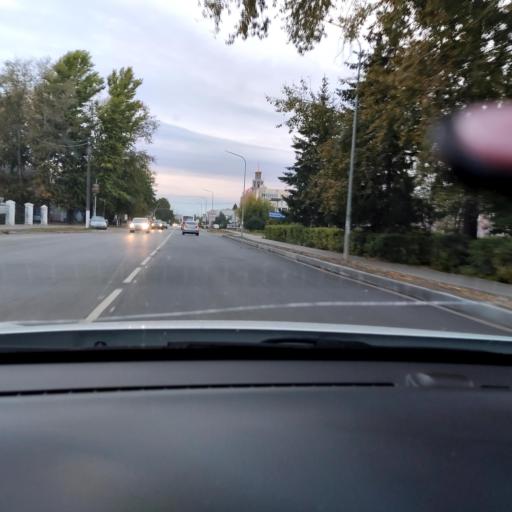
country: RU
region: Mariy-El
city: Volzhsk
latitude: 55.8632
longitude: 48.3674
